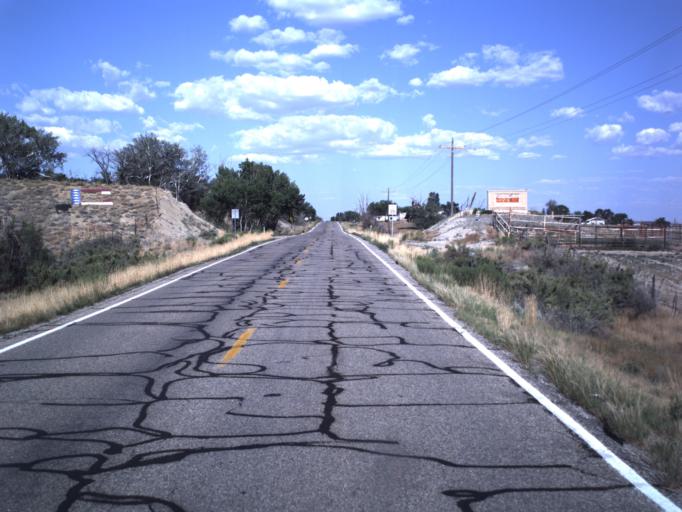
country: US
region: Utah
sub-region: Emery County
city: Huntington
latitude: 39.3479
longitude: -110.8672
